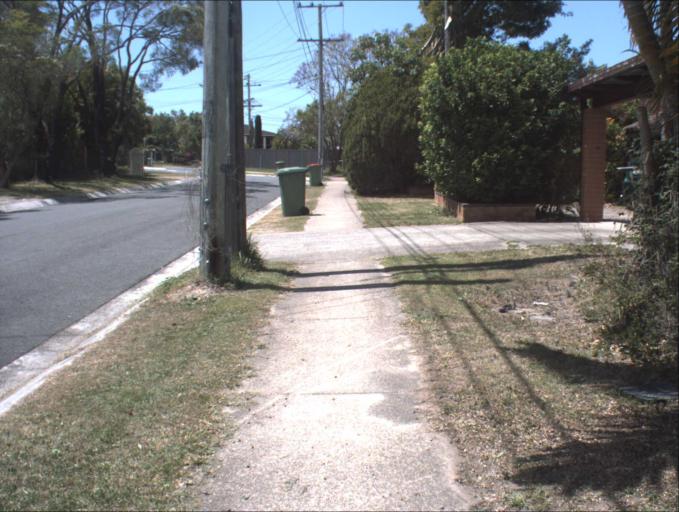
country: AU
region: Queensland
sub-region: Logan
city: Logan City
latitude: -27.6531
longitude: 153.1041
